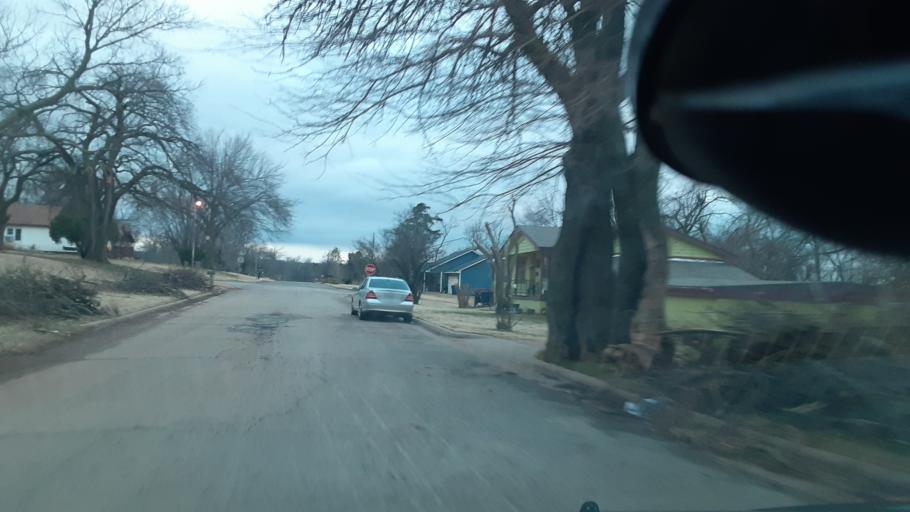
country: US
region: Oklahoma
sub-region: Logan County
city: Guthrie
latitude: 35.8745
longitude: -97.4150
